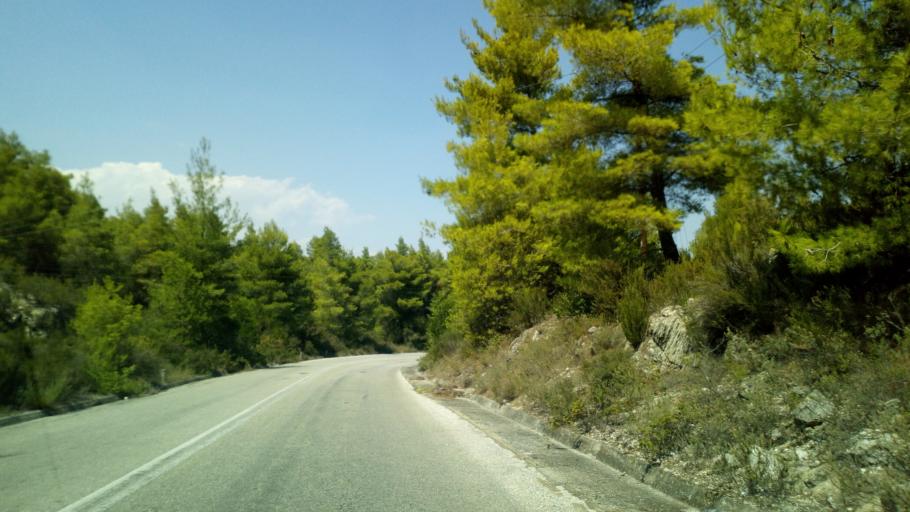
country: GR
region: Central Macedonia
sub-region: Nomos Chalkidikis
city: Sarti
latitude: 40.1406
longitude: 23.9223
